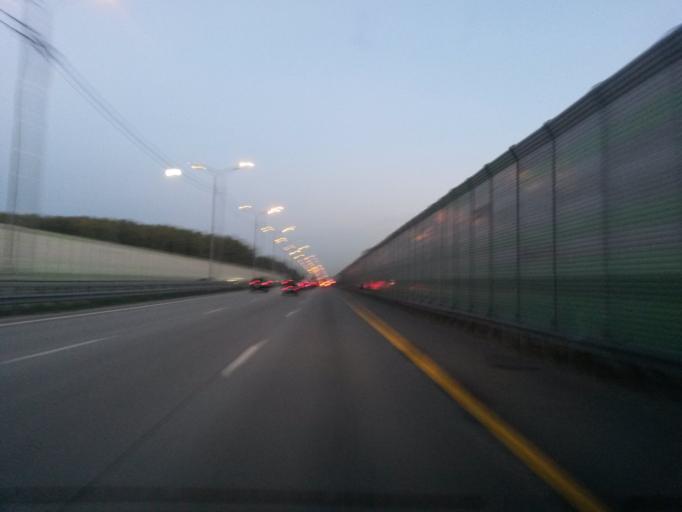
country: RU
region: Moskovskaya
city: Belyye Stolby
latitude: 55.3066
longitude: 37.8286
